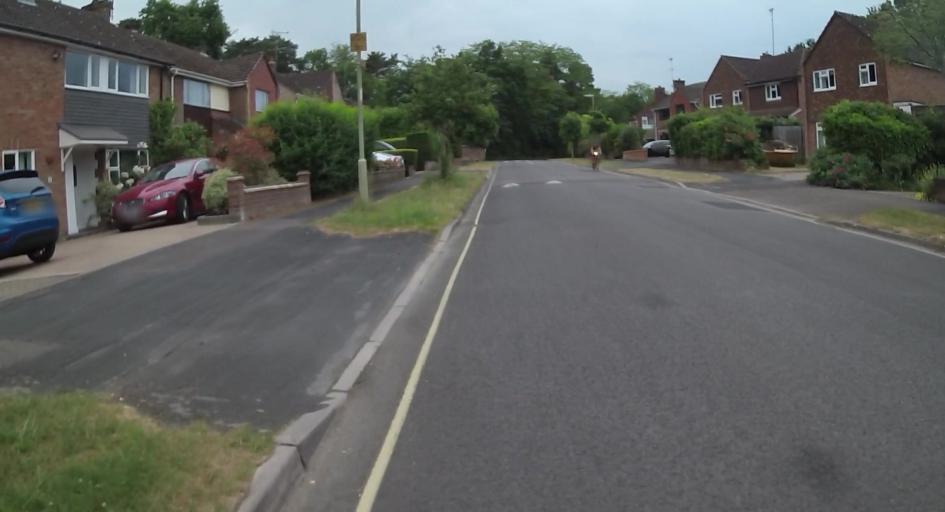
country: GB
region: England
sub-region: Hampshire
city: Fleet
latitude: 51.2762
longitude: -0.8444
